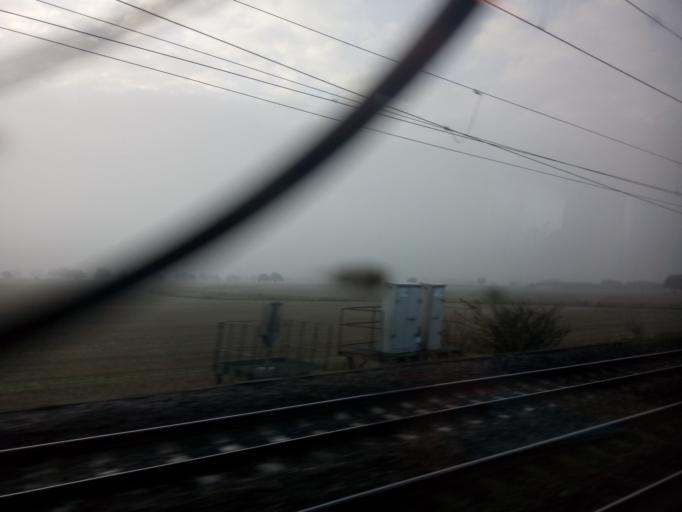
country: GB
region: England
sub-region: City of York
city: Copmanthorpe
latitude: 53.8972
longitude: -1.1589
